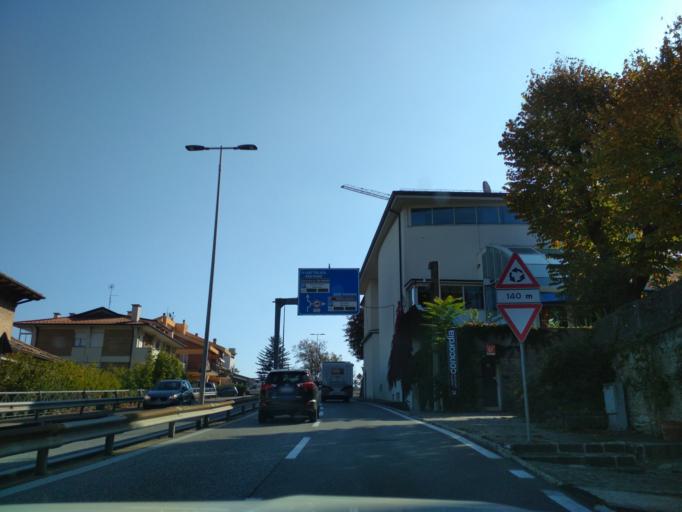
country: SM
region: Borgo Maggiore
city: Borgo Maggiore
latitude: 43.9402
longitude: 12.4474
